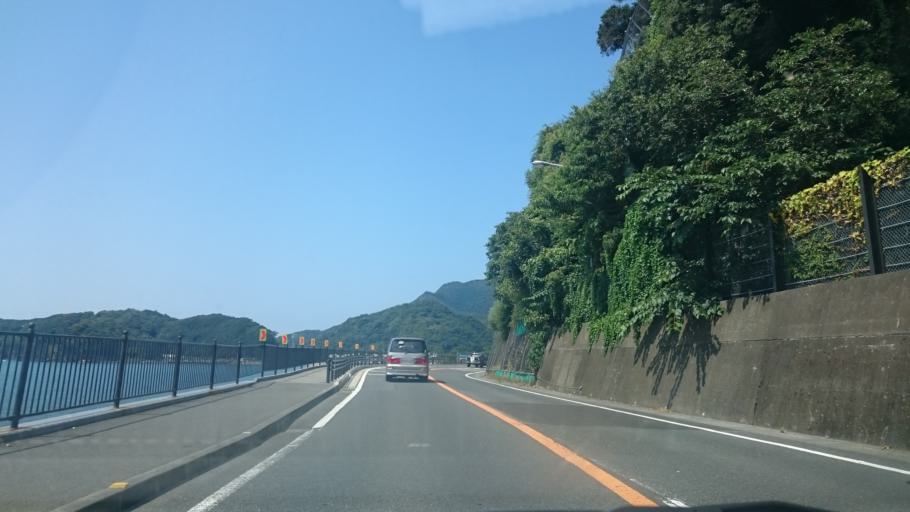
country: JP
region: Shizuoka
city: Shimoda
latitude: 34.7629
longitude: 138.7757
